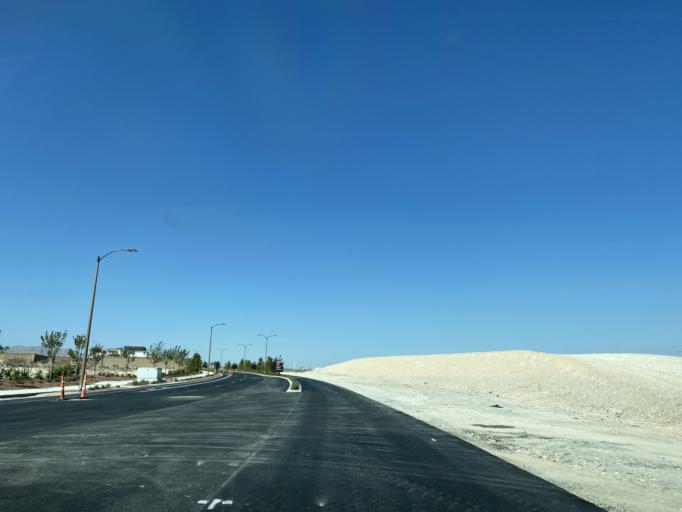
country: US
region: Nevada
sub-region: Clark County
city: Summerlin South
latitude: 36.3190
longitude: -115.3078
